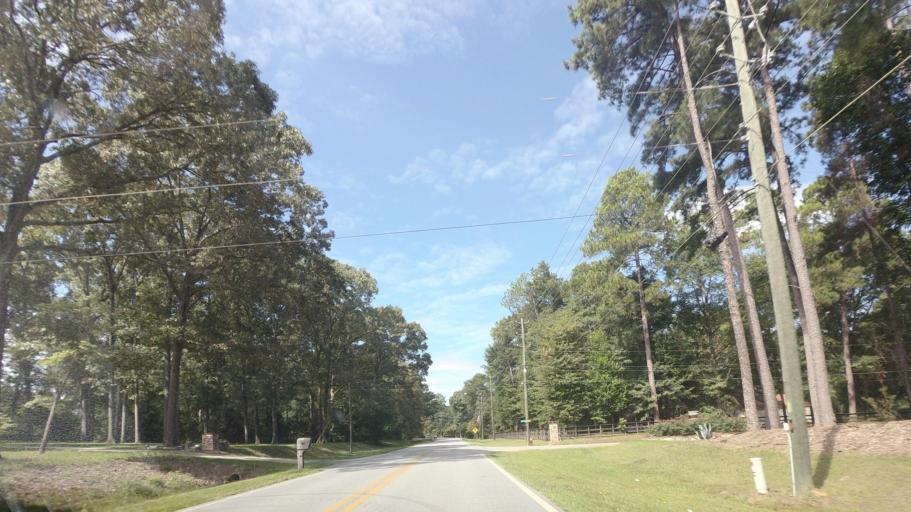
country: US
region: Georgia
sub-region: Houston County
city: Centerville
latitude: 32.6024
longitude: -83.7060
